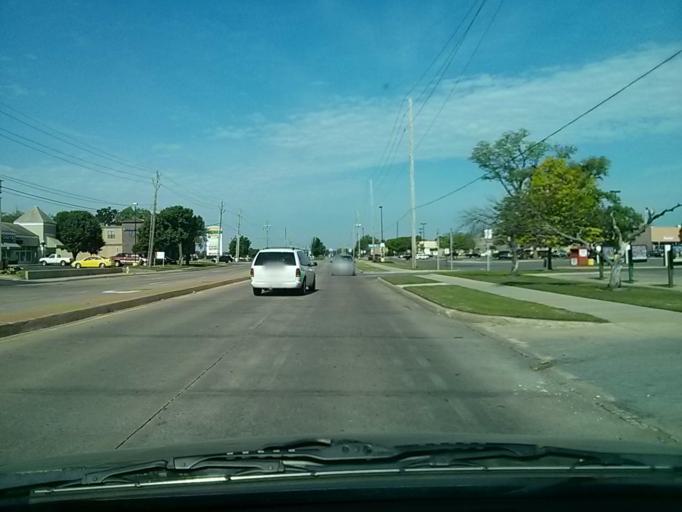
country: US
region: Oklahoma
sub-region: Tulsa County
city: Jenks
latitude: 36.0465
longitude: -95.9582
